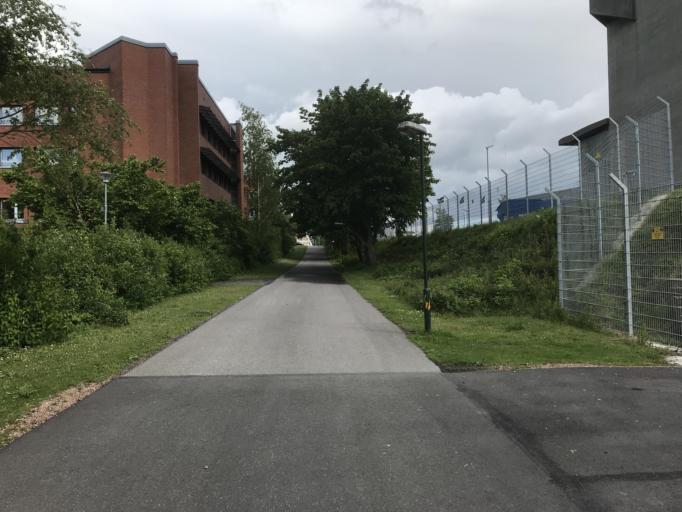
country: SE
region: Skane
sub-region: Malmo
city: Oxie
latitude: 55.5736
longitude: 13.0565
